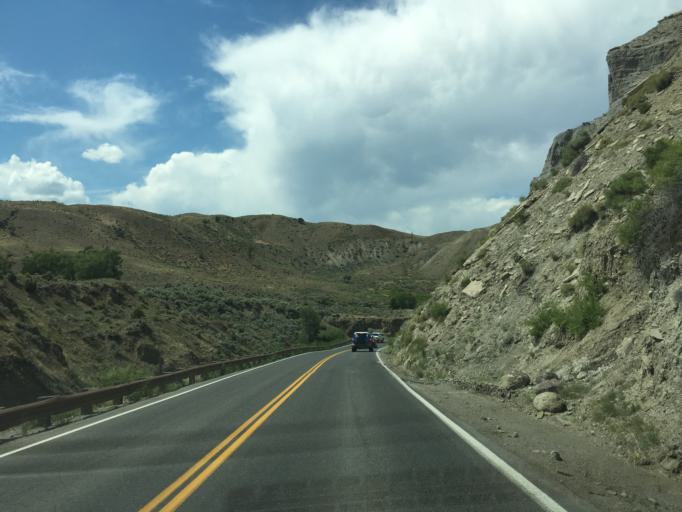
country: US
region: Montana
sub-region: Gallatin County
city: West Yellowstone
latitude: 45.0054
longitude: -110.6923
